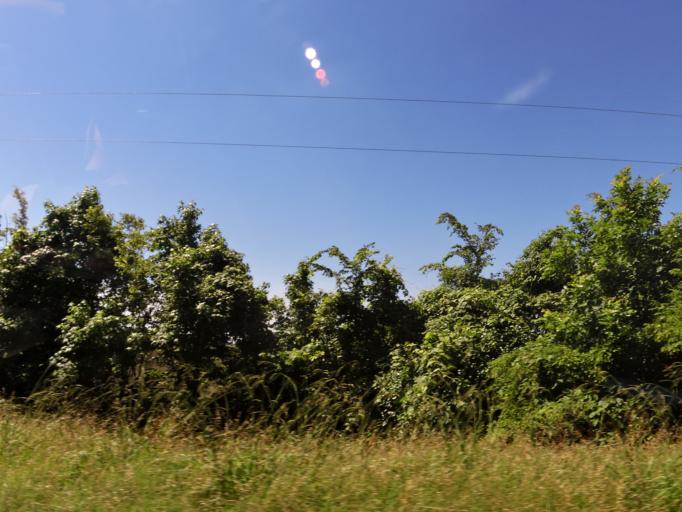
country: US
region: Missouri
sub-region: New Madrid County
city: Lilbourn
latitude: 36.5552
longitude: -89.6628
